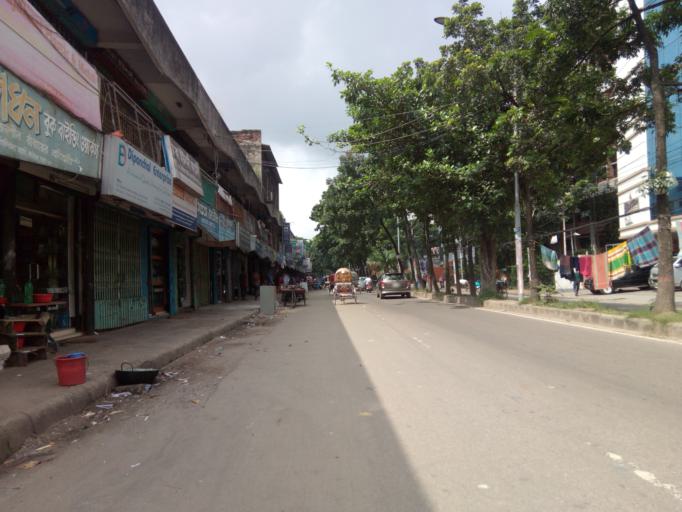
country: BD
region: Dhaka
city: Azimpur
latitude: 23.7354
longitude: 90.3886
